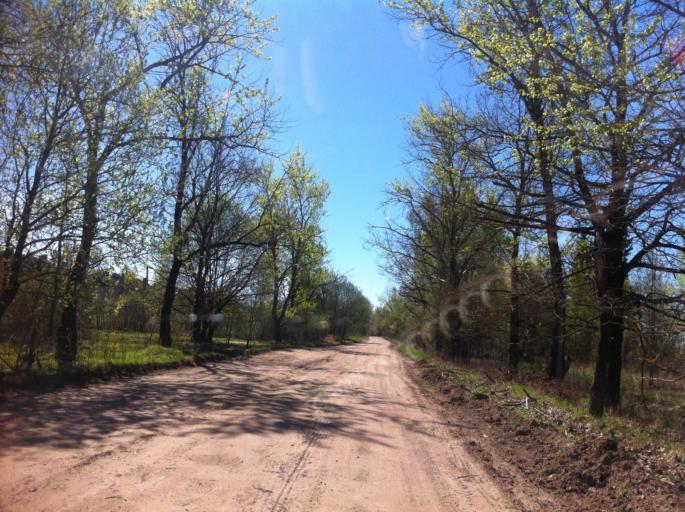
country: RU
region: Pskov
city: Izborsk
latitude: 57.7863
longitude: 27.9627
